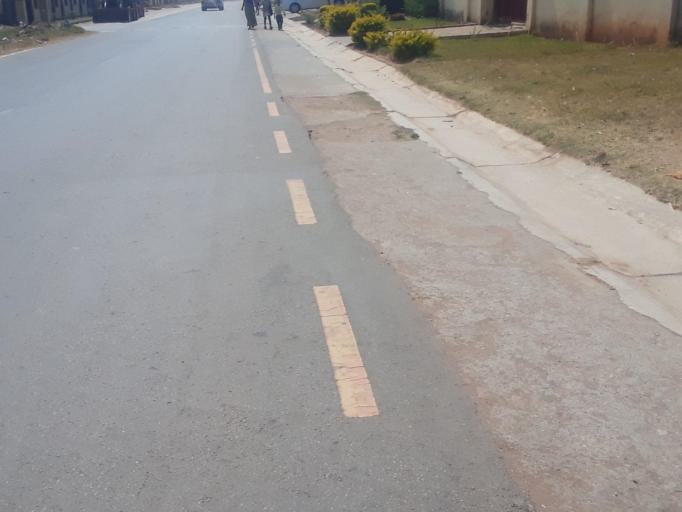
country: ZM
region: Lusaka
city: Lusaka
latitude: -15.3590
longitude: 28.2808
